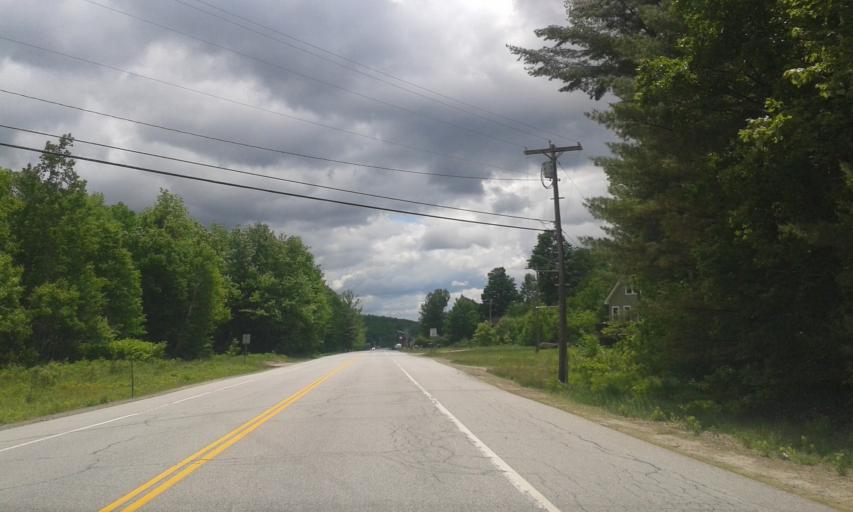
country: US
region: New Hampshire
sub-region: Grafton County
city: Woodstock
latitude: 44.0811
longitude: -71.6851
